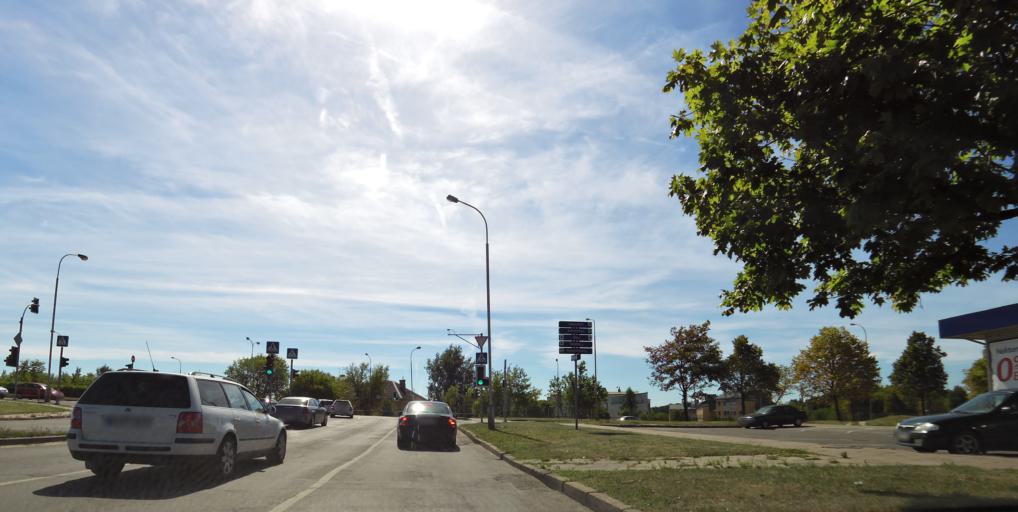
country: LT
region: Vilnius County
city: Seskine
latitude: 54.7107
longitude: 25.2490
